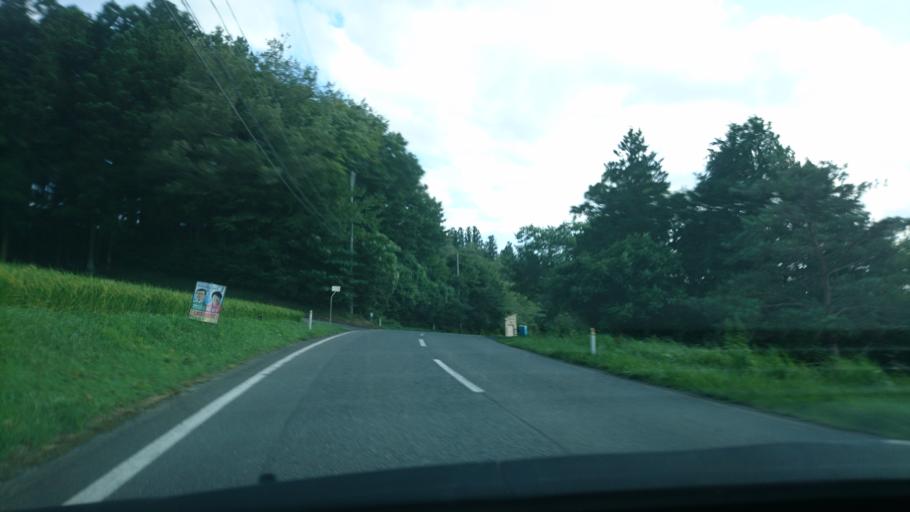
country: JP
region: Iwate
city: Ichinoseki
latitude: 39.0228
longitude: 141.2915
